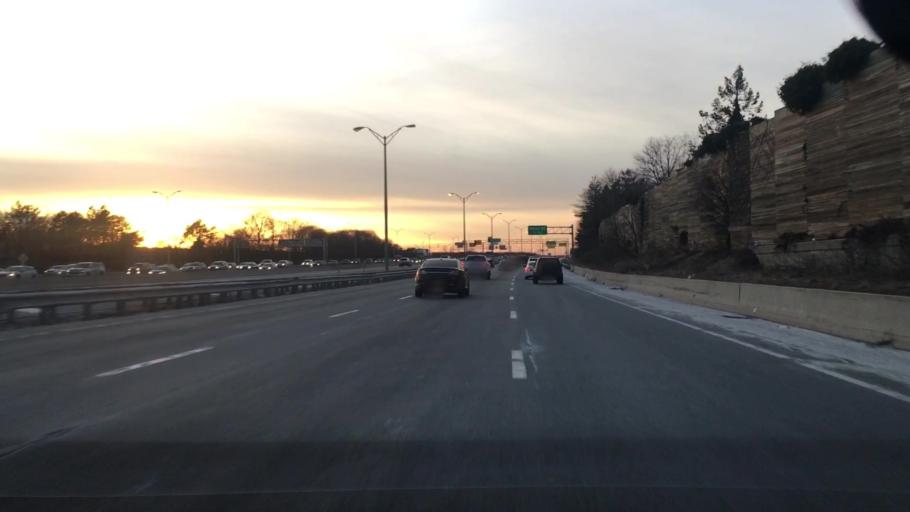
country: US
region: New York
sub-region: Suffolk County
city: Brentwood
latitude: 40.8052
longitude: -73.2588
